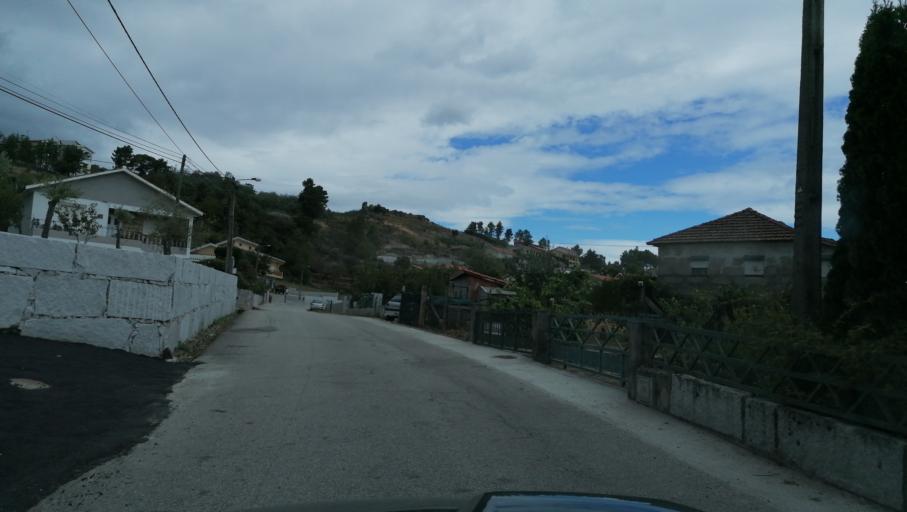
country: PT
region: Vila Real
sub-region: Vila Pouca de Aguiar
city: Vila Pouca de Aguiar
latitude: 41.5511
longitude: -7.6213
